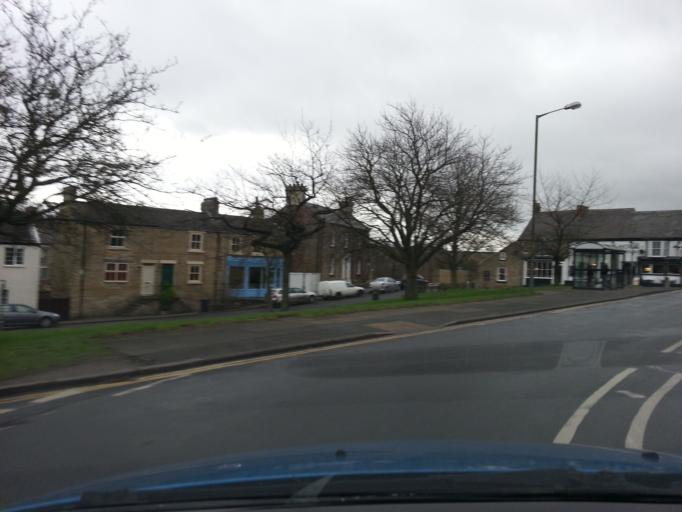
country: GB
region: England
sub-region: County Durham
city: Crook
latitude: 54.7155
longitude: -1.7436
